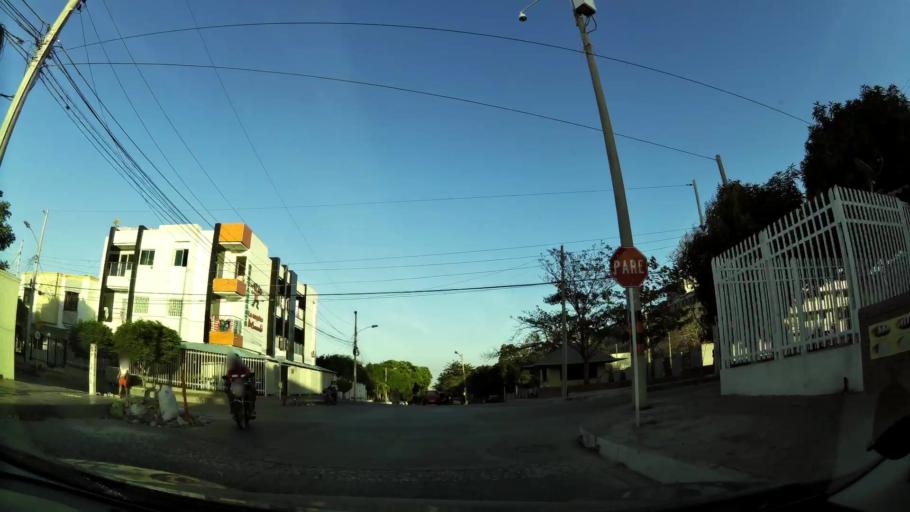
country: CO
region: Atlantico
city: Barranquilla
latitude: 10.9727
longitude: -74.8013
